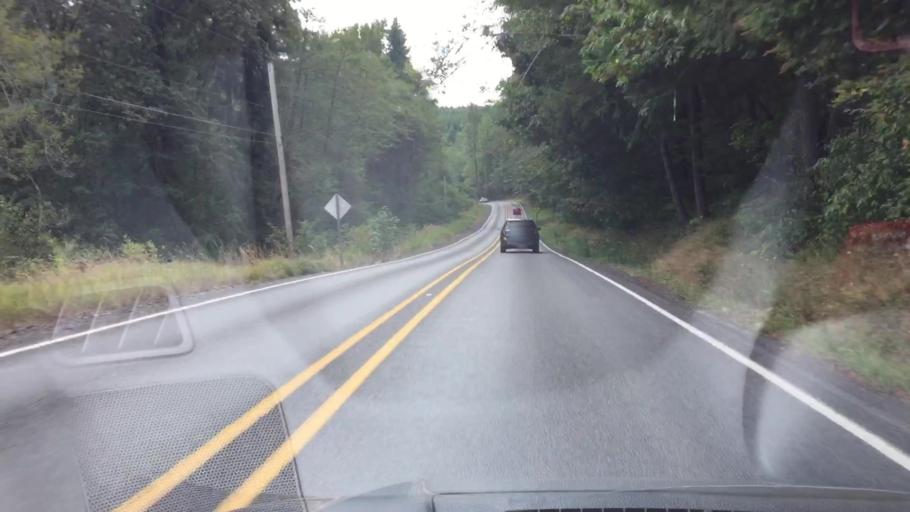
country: US
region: Washington
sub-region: Pierce County
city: Eatonville
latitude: 46.8401
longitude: -122.2489
